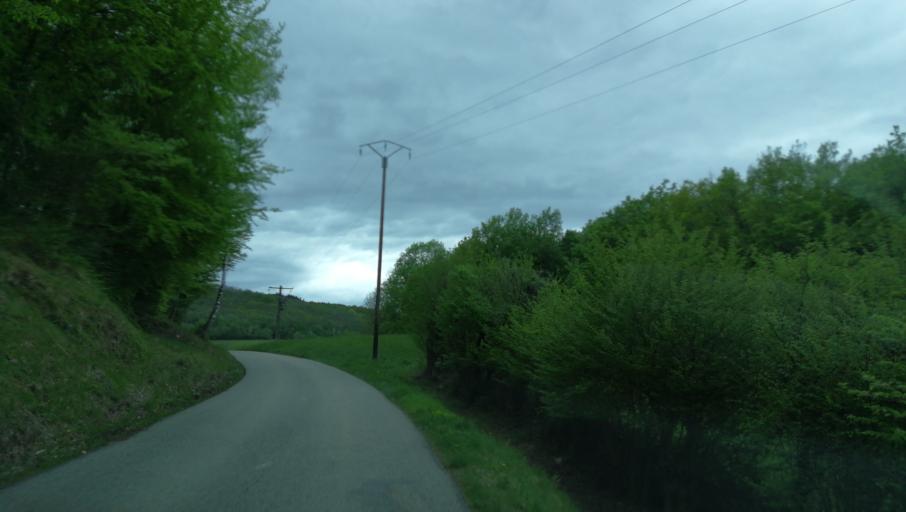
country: FR
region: Rhone-Alpes
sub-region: Departement de la Savoie
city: Chatillon
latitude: 45.7853
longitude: 5.8201
